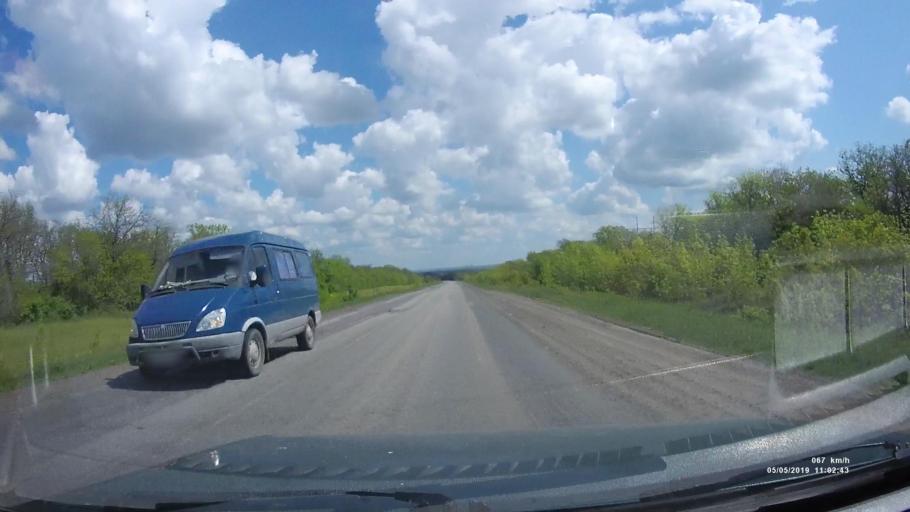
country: RU
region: Rostov
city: Ust'-Donetskiy
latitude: 47.6864
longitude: 40.9114
